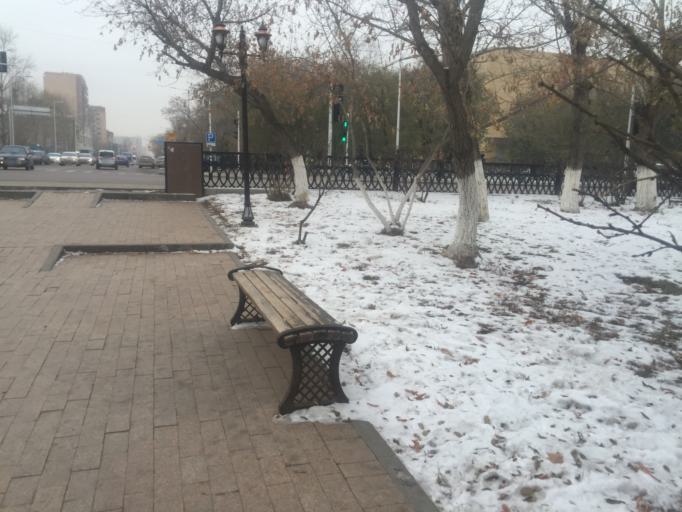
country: KZ
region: Astana Qalasy
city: Astana
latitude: 51.1829
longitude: 71.4202
